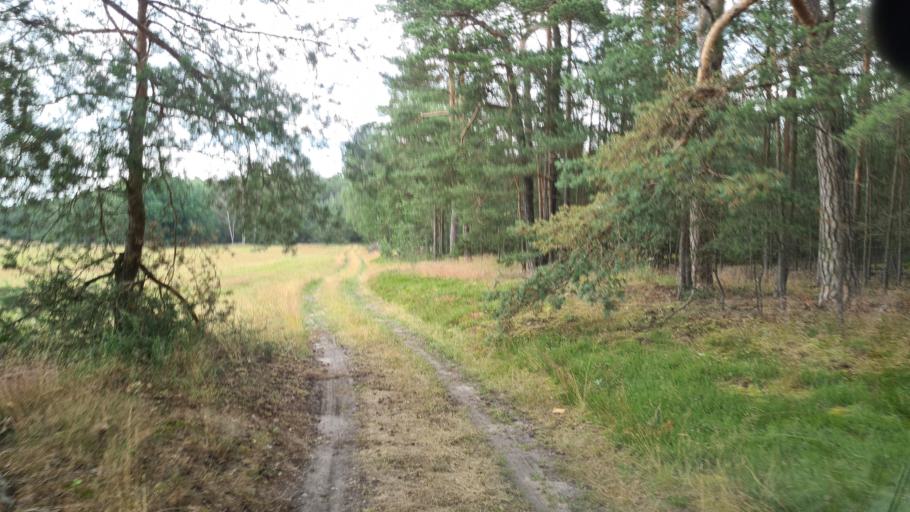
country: DE
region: Brandenburg
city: Crinitz
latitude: 51.7133
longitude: 13.8259
